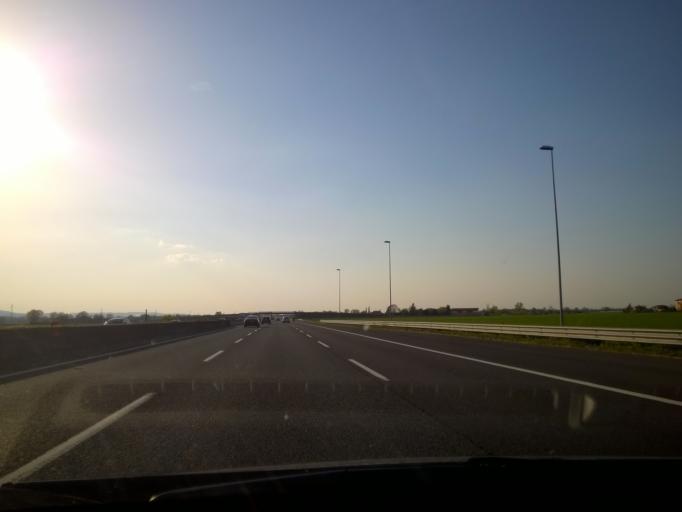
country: IT
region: Emilia-Romagna
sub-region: Provincia di Bologna
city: Castel San Pietro Terme
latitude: 44.4317
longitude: 11.5895
